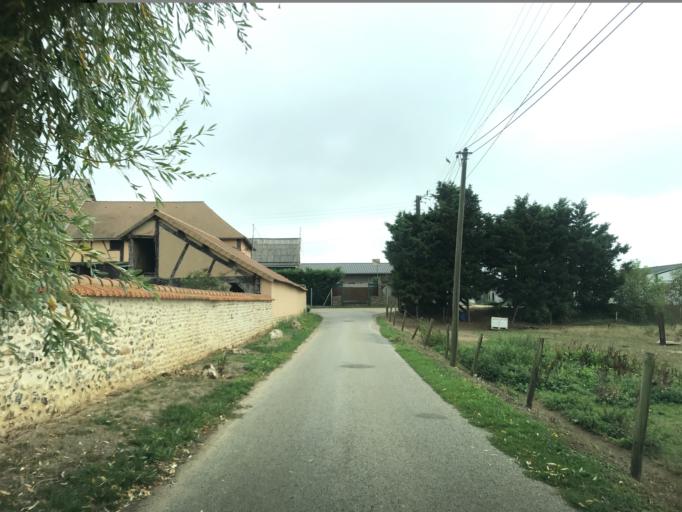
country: FR
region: Haute-Normandie
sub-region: Departement de l'Eure
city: Houlbec-Cocherel
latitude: 49.0537
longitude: 1.3530
